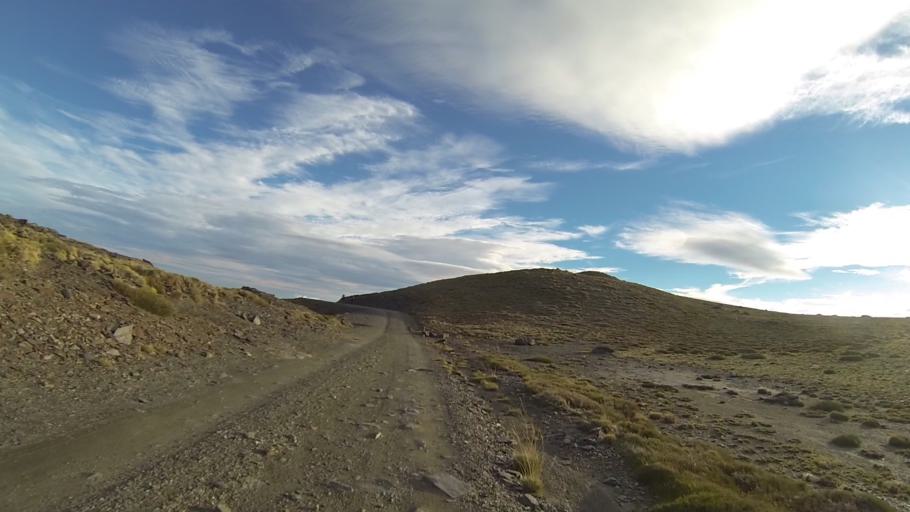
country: ES
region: Andalusia
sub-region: Provincia de Granada
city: Trevelez
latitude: 36.9970
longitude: -3.3121
